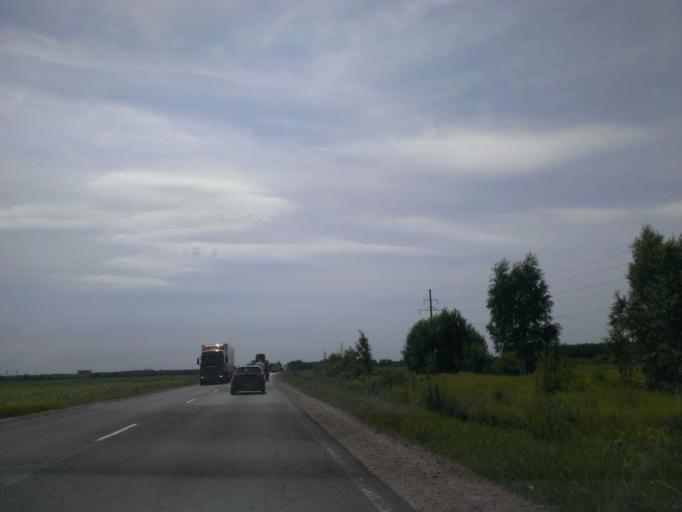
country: LV
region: Salaspils
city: Salaspils
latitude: 56.8634
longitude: 24.4057
